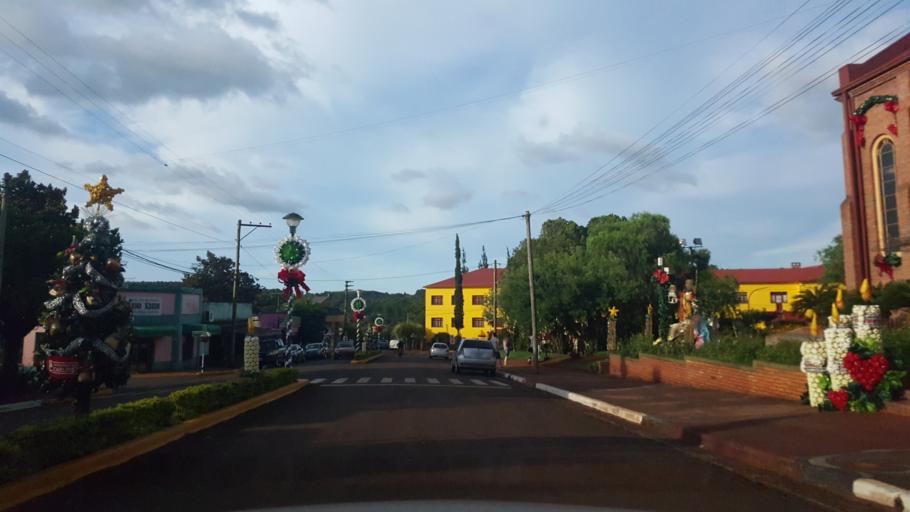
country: AR
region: Misiones
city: Capiovi
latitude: -26.9273
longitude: -55.0577
